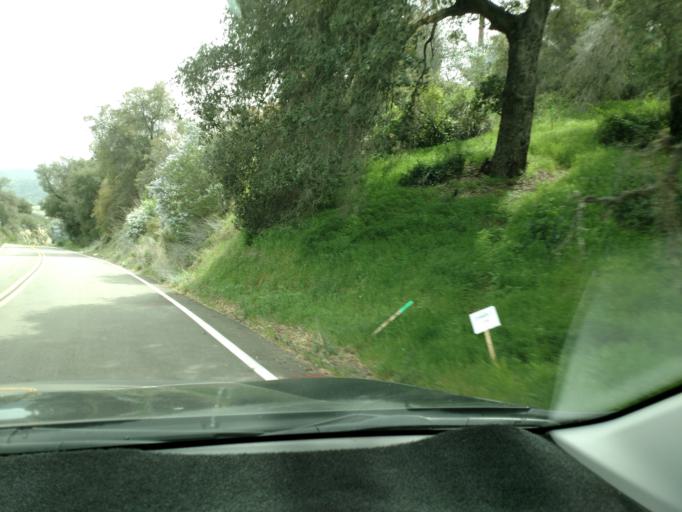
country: US
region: California
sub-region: Riverside County
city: Aguanga
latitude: 33.2442
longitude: -116.7640
